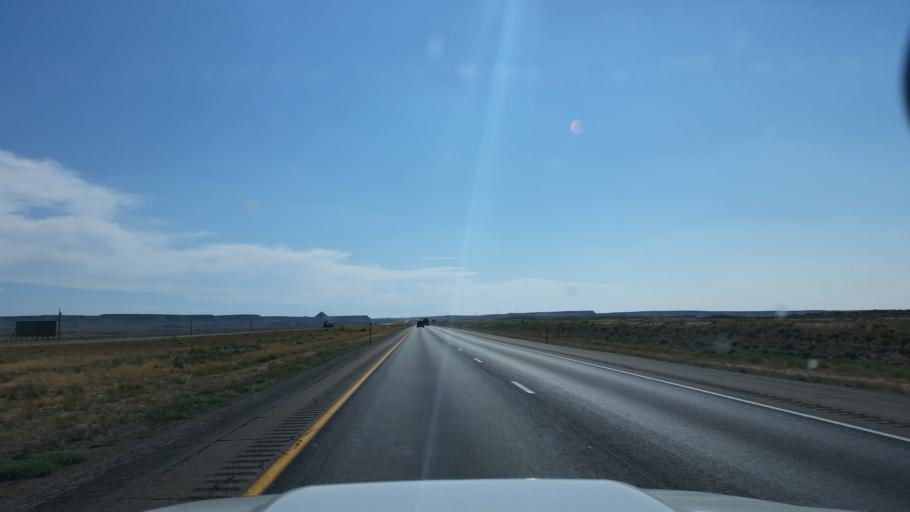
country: US
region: Wyoming
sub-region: Uinta County
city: Lyman
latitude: 41.5180
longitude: -109.9692
